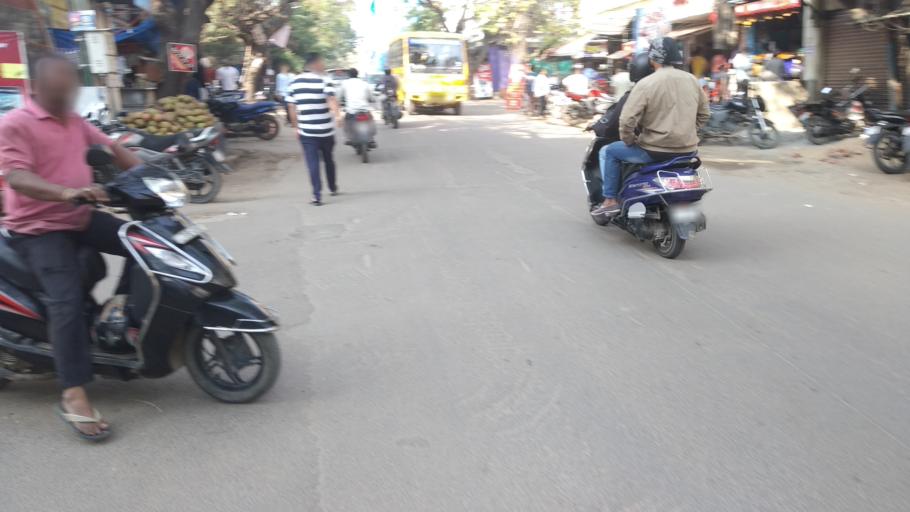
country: IN
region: Telangana
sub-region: Rangareddi
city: Kukatpalli
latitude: 17.4438
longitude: 78.4463
